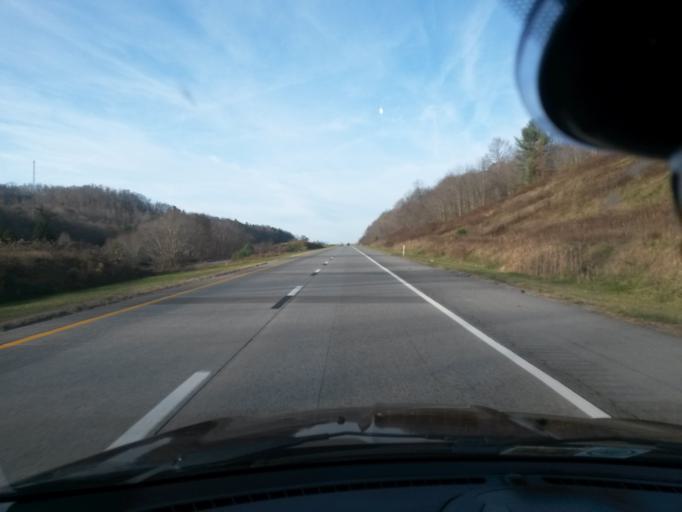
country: US
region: West Virginia
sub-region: Greenbrier County
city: Rainelle
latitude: 37.8420
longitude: -80.7421
